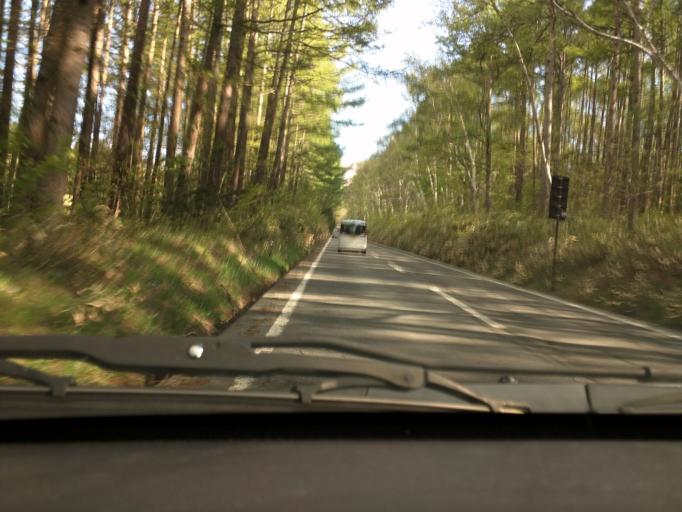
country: JP
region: Nagano
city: Nagano-shi
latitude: 36.7054
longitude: 138.1335
